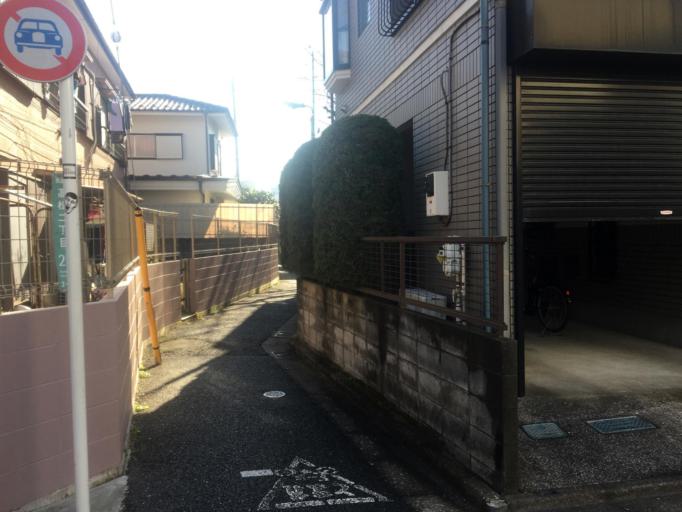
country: JP
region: Tokyo
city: Tokyo
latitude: 35.7382
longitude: 139.6980
